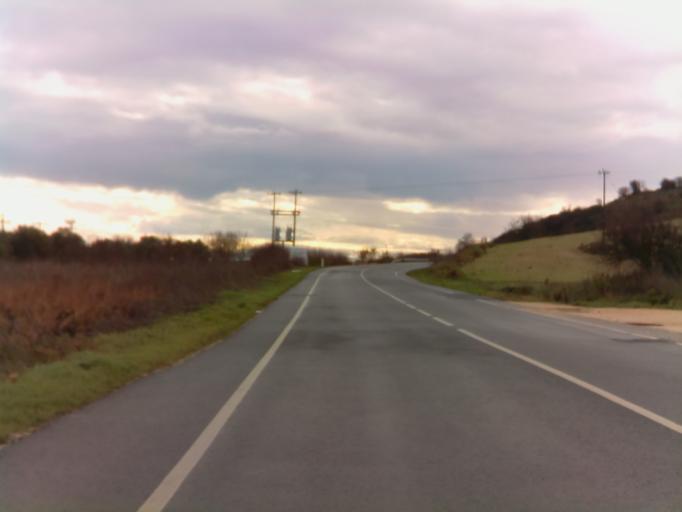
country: CY
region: Pafos
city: Pegeia
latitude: 34.9075
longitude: 32.4387
